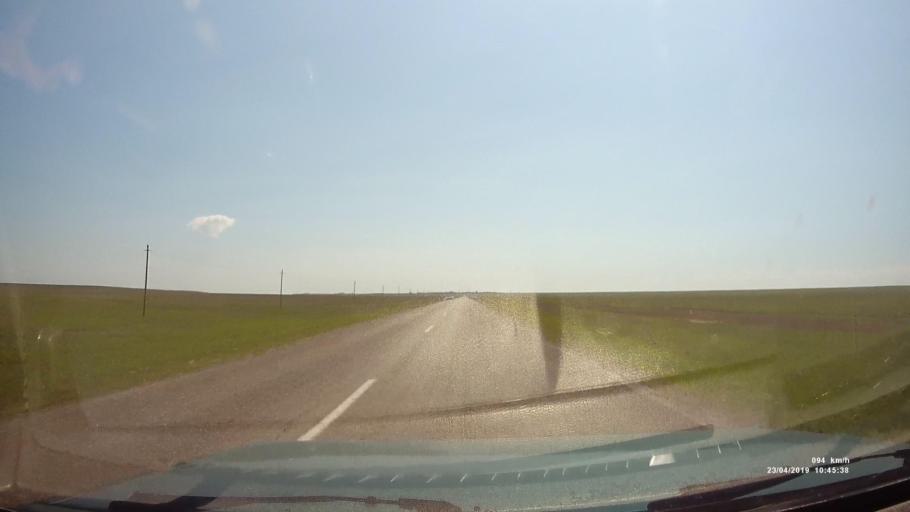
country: RU
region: Kalmykiya
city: Yashalta
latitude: 46.4497
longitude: 42.6777
